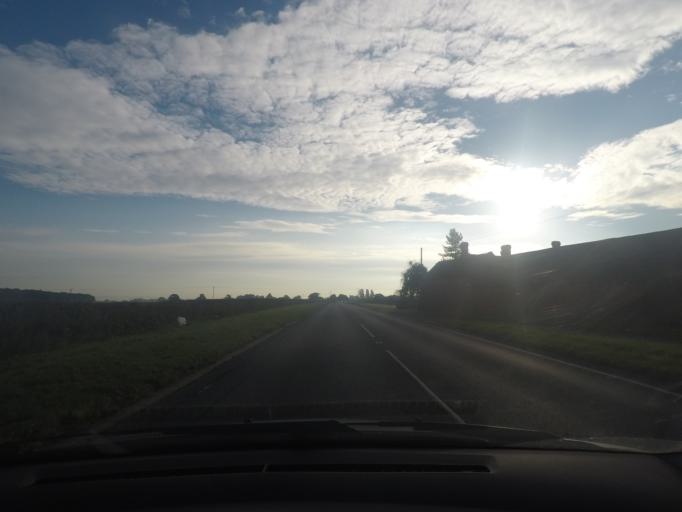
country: GB
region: England
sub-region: City of York
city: Elvington
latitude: 53.9517
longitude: -0.9491
